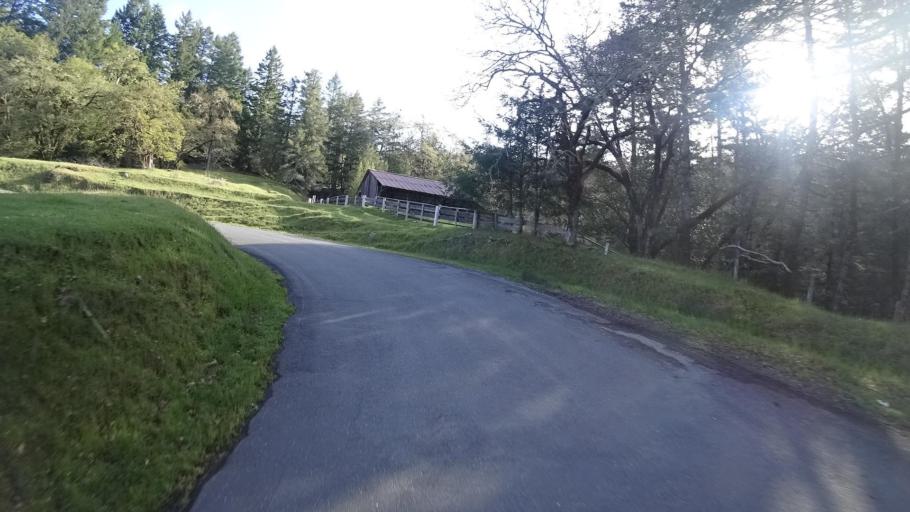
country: US
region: California
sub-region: Humboldt County
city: Blue Lake
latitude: 40.7088
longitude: -123.9363
